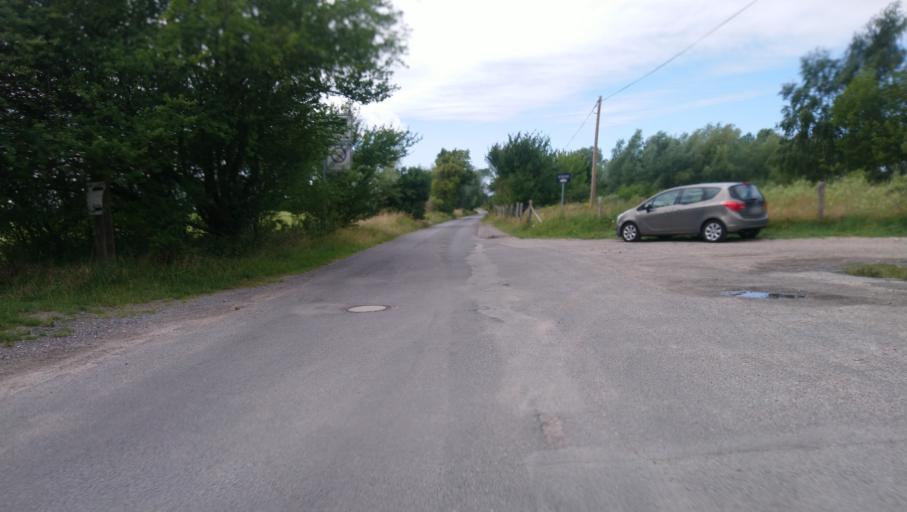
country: DE
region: Mecklenburg-Vorpommern
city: Elmenhorst
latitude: 54.1705
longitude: 12.0261
